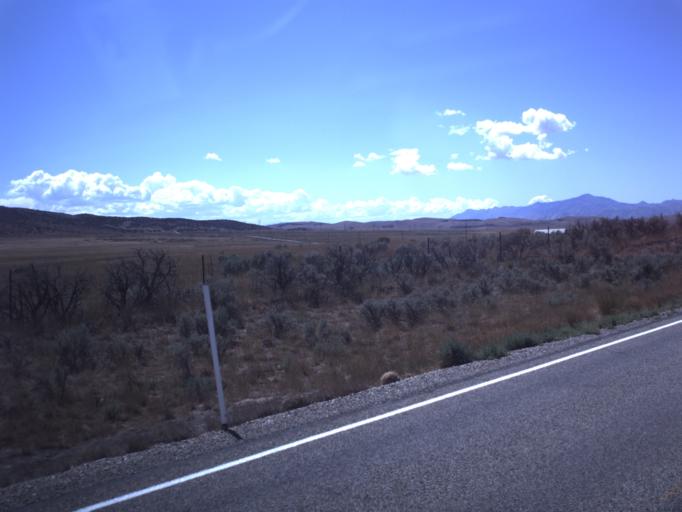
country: US
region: Utah
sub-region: Juab County
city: Nephi
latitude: 39.6877
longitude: -112.0041
